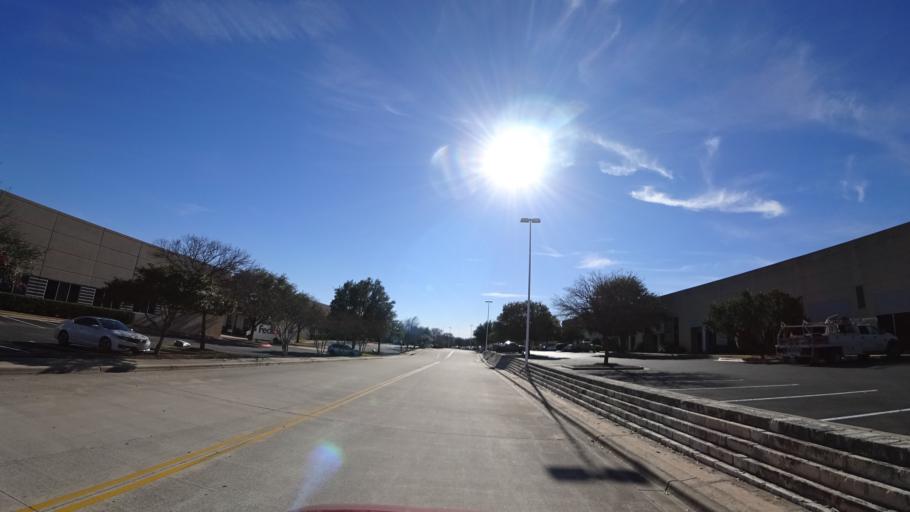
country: US
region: Texas
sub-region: Travis County
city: Wells Branch
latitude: 30.3864
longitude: -97.7096
